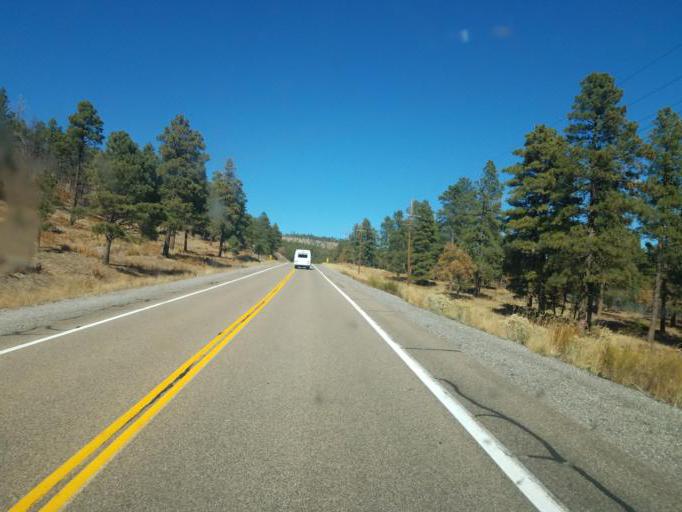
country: US
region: New Mexico
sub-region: Los Alamos County
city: Los Alamos
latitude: 35.8566
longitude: -106.3534
